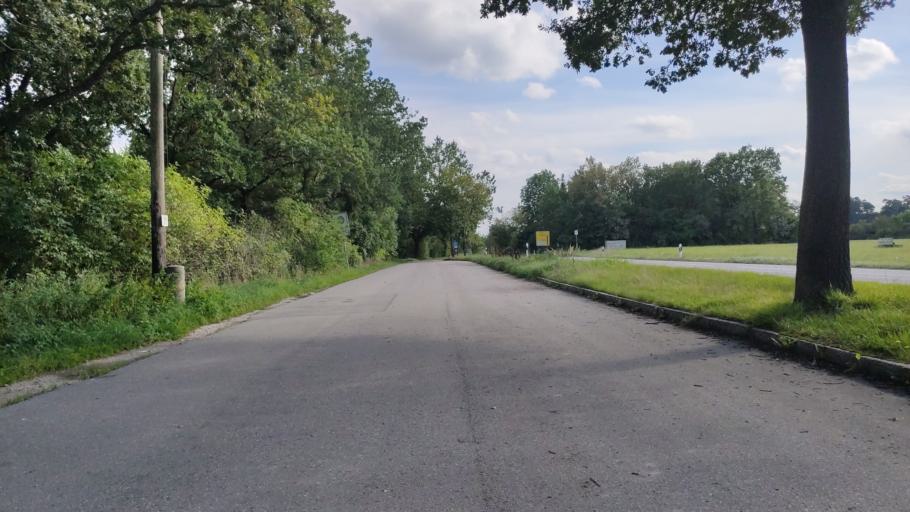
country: DE
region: Bavaria
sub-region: Upper Bavaria
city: Hurlach
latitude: 48.1150
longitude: 10.8486
